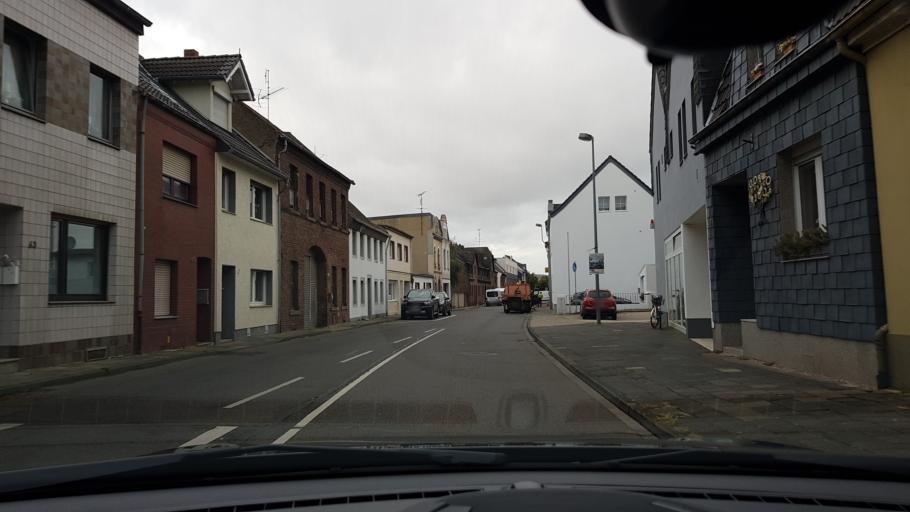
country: DE
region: North Rhine-Westphalia
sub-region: Regierungsbezirk Koln
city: Elsdorf
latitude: 50.9345
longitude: 6.5717
